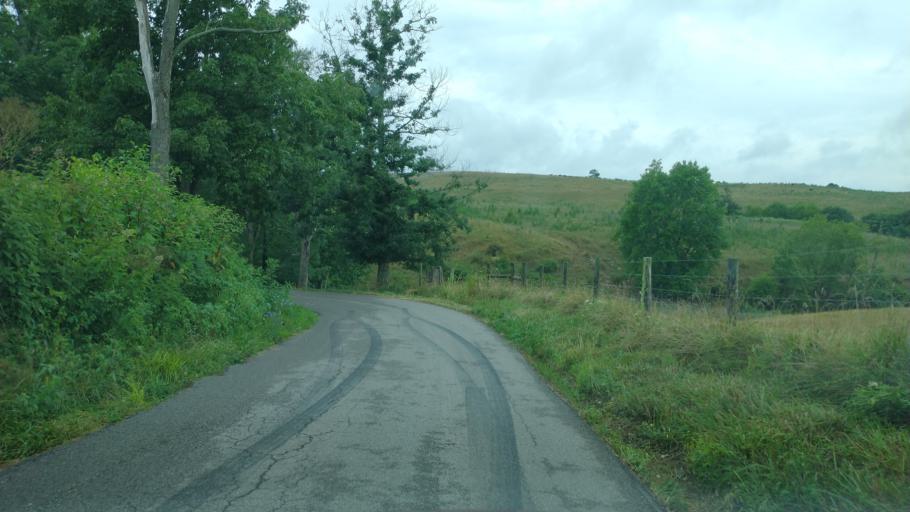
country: US
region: West Virginia
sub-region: Mason County
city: New Haven
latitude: 38.9261
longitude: -81.9660
